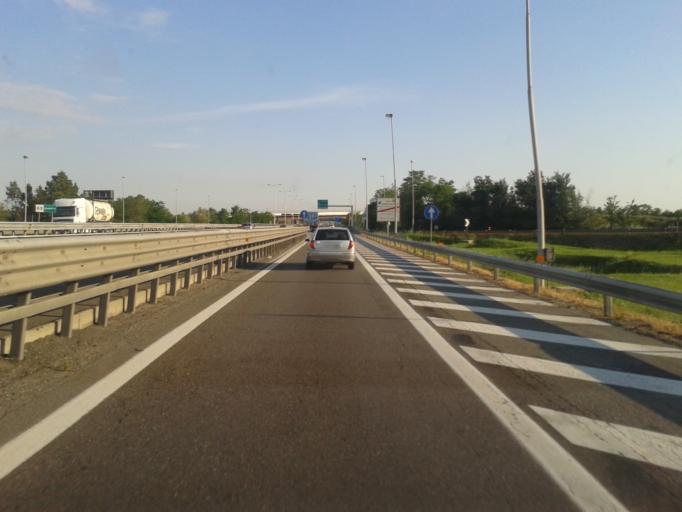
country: IT
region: Piedmont
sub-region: Provincia di Alessandria
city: Tortona
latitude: 44.9150
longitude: 8.8440
